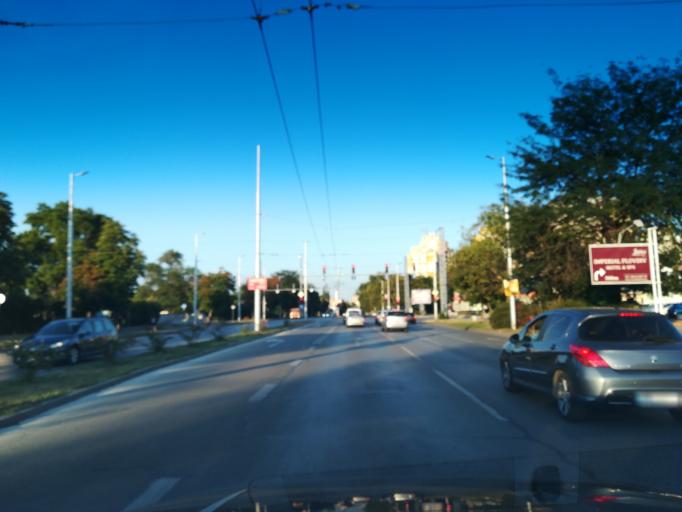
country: BG
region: Plovdiv
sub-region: Obshtina Plovdiv
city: Plovdiv
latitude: 42.1479
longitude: 24.7689
